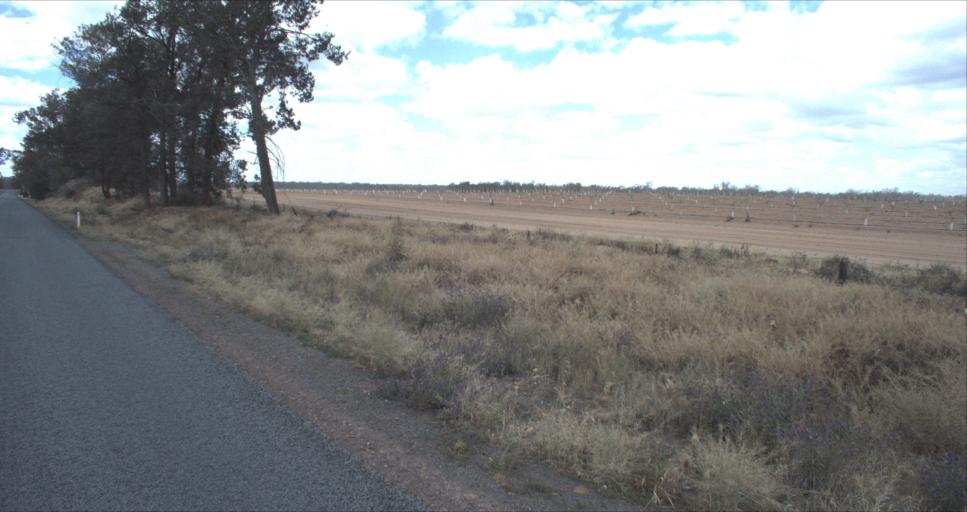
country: AU
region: New South Wales
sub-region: Leeton
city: Leeton
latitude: -34.6569
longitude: 146.3501
